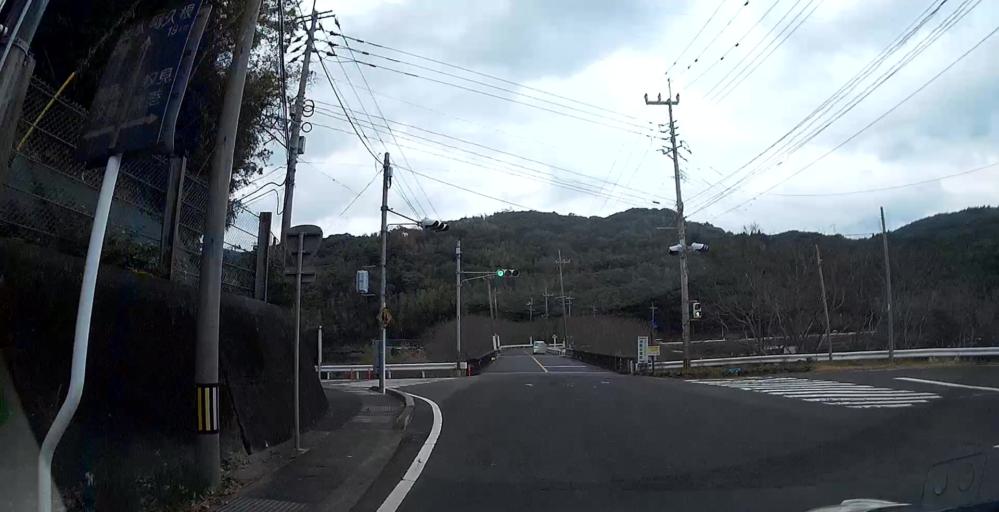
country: JP
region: Kagoshima
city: Akune
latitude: 32.1105
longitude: 130.1435
